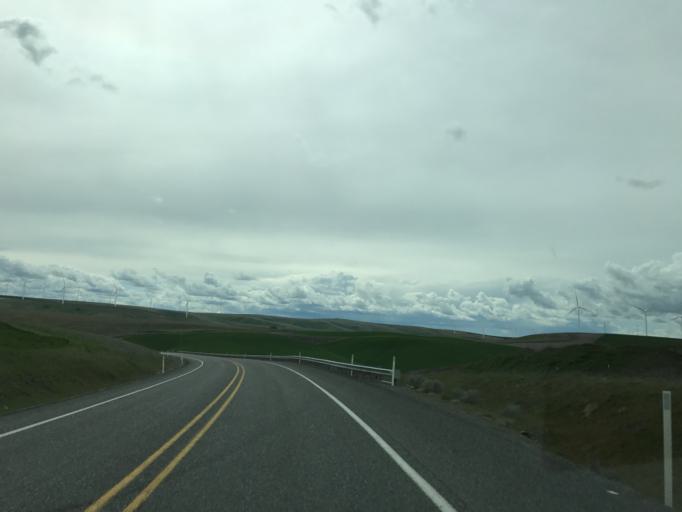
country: US
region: Washington
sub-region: Garfield County
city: Pomeroy
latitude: 46.5312
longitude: -117.7841
